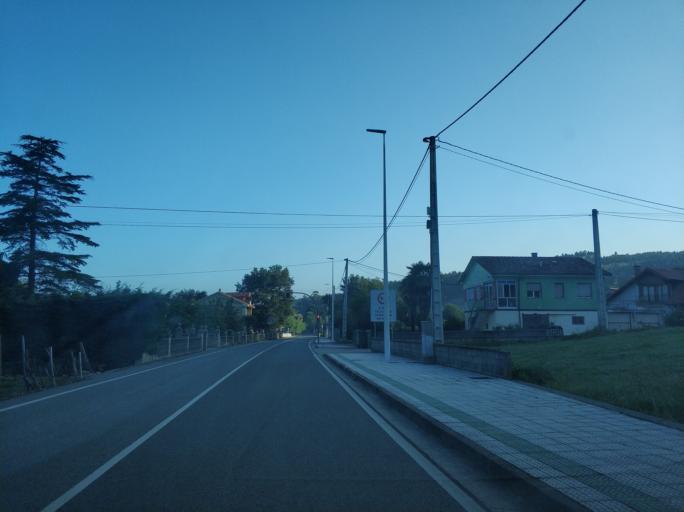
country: ES
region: Cantabria
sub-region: Provincia de Cantabria
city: Polanco
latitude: 43.3651
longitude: -3.9578
